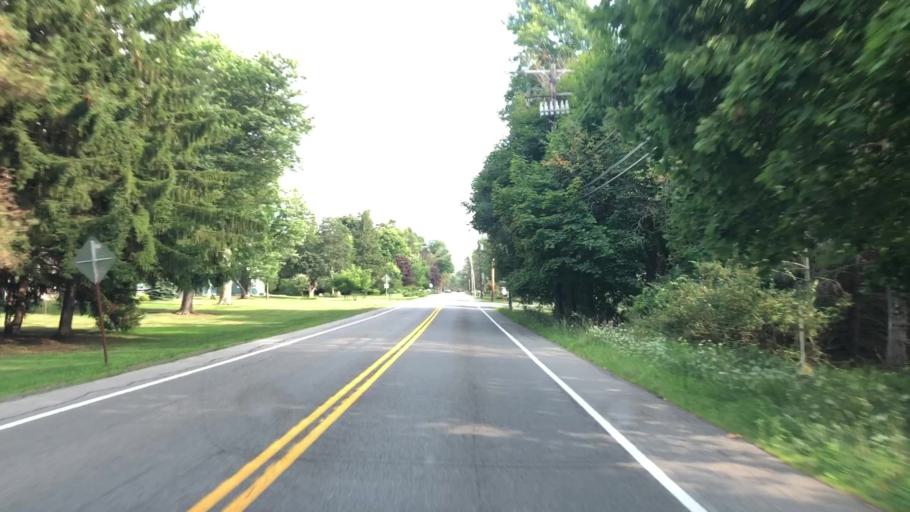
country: US
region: New York
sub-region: Erie County
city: Elma Center
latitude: 42.8465
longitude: -78.6413
